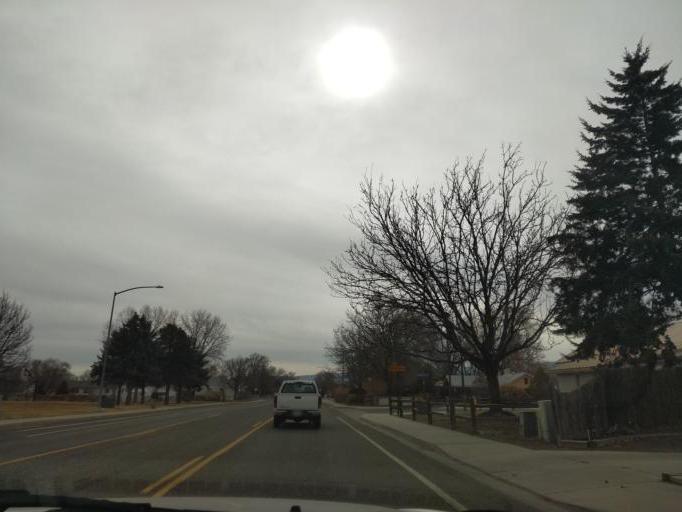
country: US
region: Colorado
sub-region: Mesa County
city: Grand Junction
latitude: 39.0834
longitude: -108.5292
